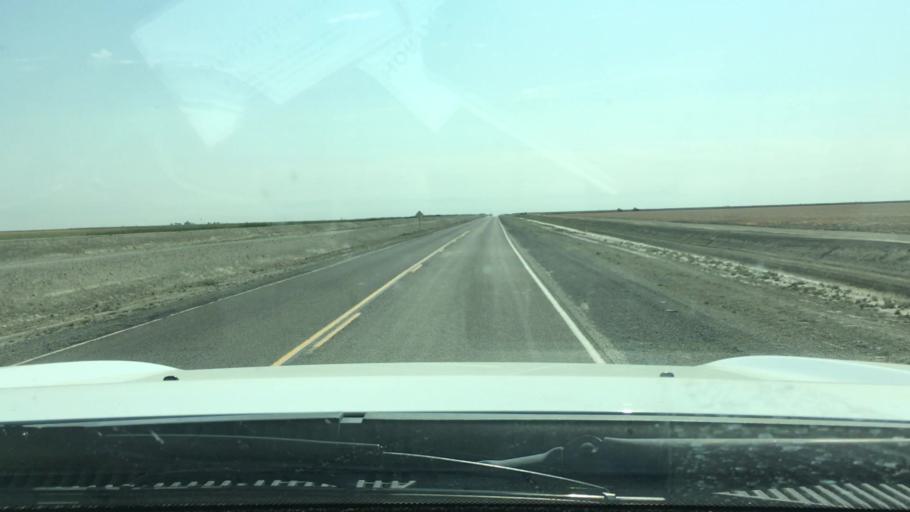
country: US
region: California
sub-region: Tulare County
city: Alpaugh
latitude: 35.9341
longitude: -119.6434
